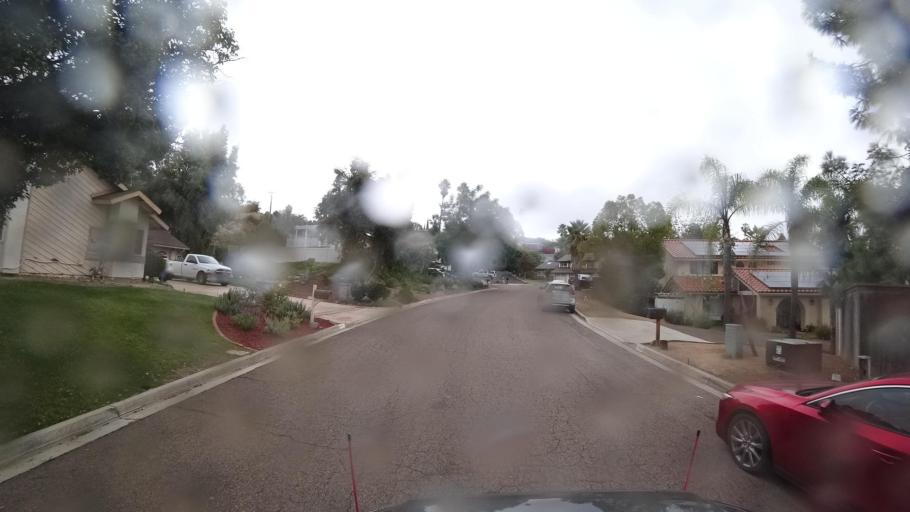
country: US
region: California
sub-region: San Diego County
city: Rancho San Diego
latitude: 32.7726
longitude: -116.9258
